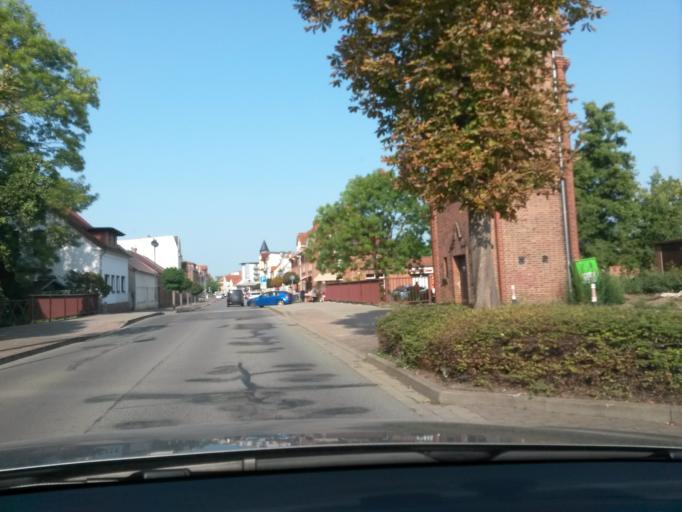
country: DE
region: Saxony-Anhalt
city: Tangerhutte
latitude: 52.4339
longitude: 11.8173
